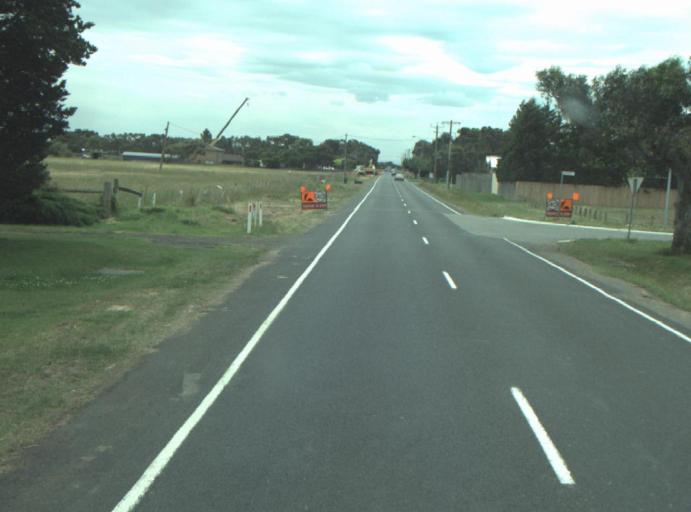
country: AU
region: Victoria
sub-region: Greater Geelong
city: Leopold
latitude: -38.1817
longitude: 144.4566
